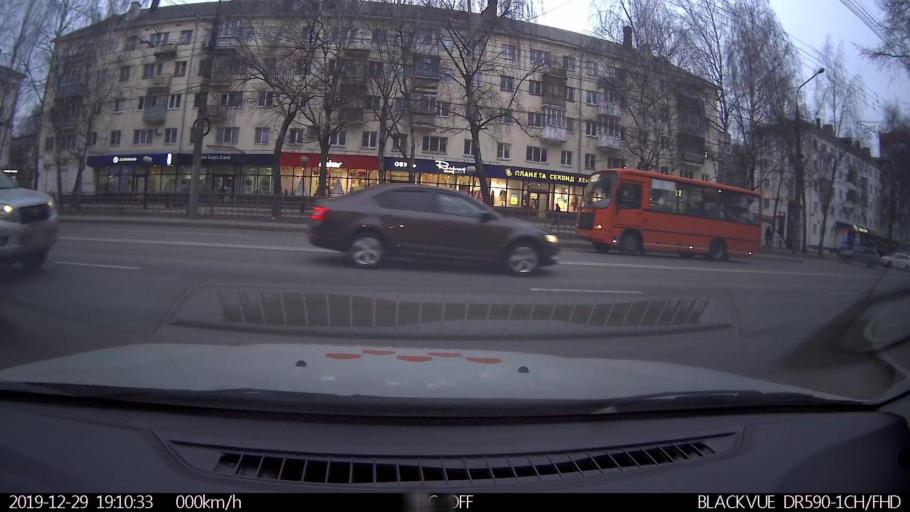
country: RU
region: Nizjnij Novgorod
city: Neklyudovo
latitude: 56.3525
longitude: 43.8673
